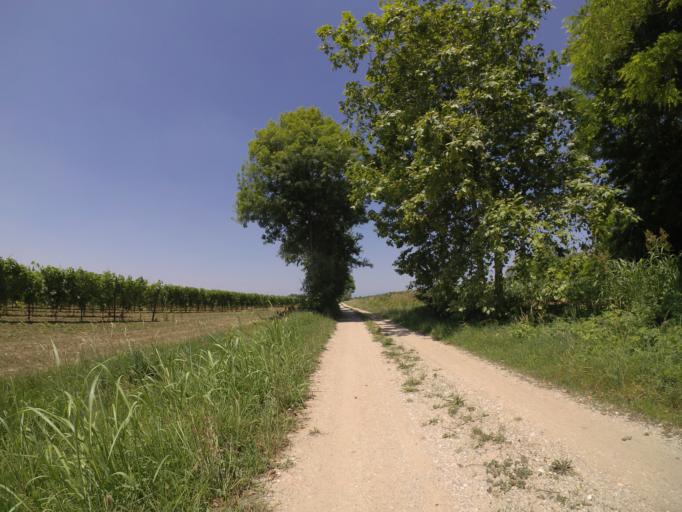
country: IT
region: Friuli Venezia Giulia
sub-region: Provincia di Udine
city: Bertiolo
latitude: 45.9405
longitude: 13.0169
